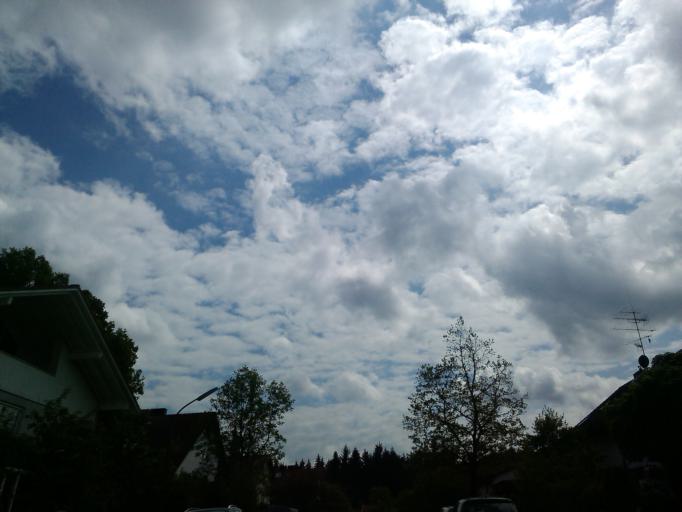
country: DE
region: Bavaria
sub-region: Upper Bavaria
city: Neuried
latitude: 48.1048
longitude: 11.4535
